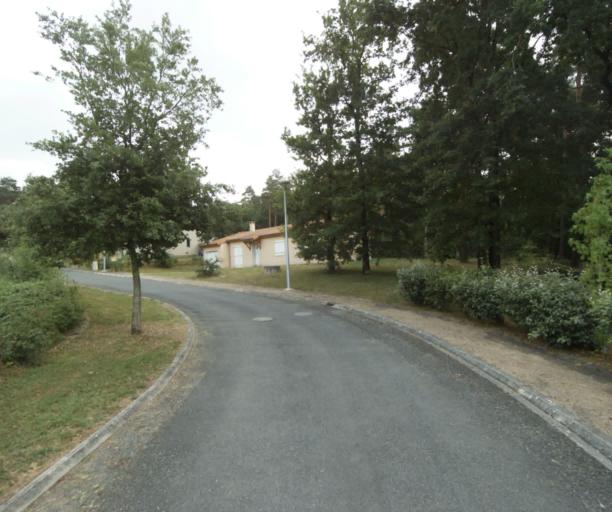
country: FR
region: Midi-Pyrenees
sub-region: Departement de la Haute-Garonne
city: Revel
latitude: 43.4320
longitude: 2.0230
